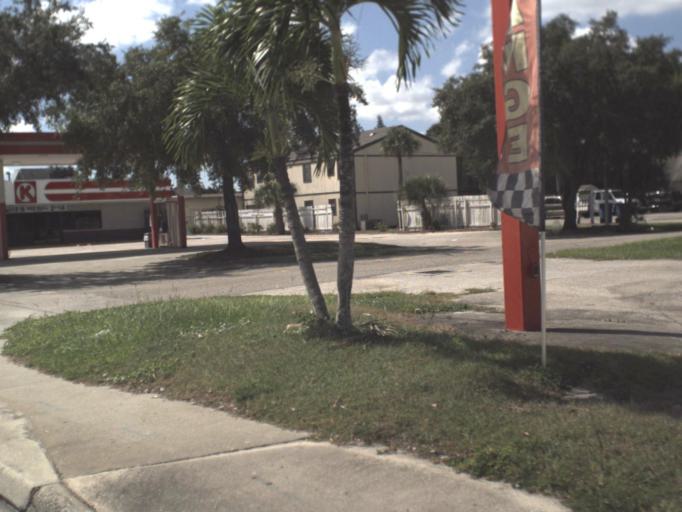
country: US
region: Florida
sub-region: Lee County
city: Fort Myers
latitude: 26.6219
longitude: -81.8723
